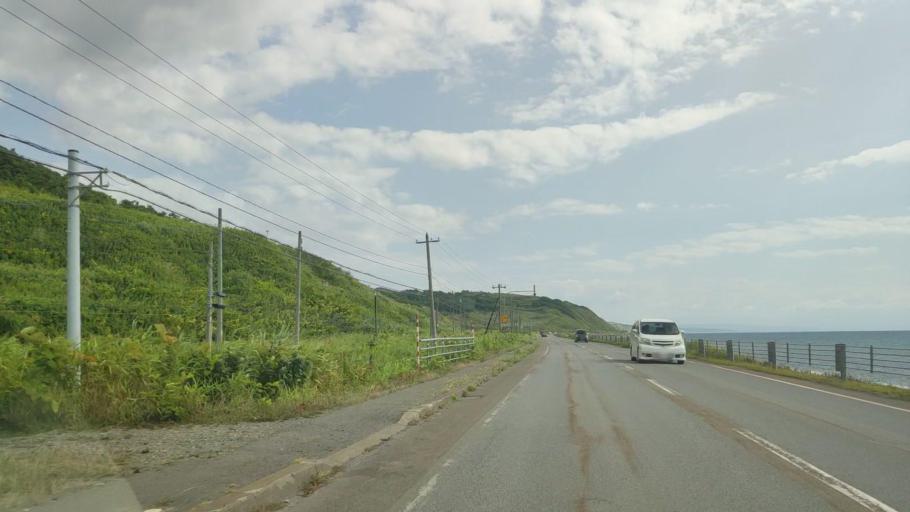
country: JP
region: Hokkaido
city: Rumoi
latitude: 44.1063
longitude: 141.6595
